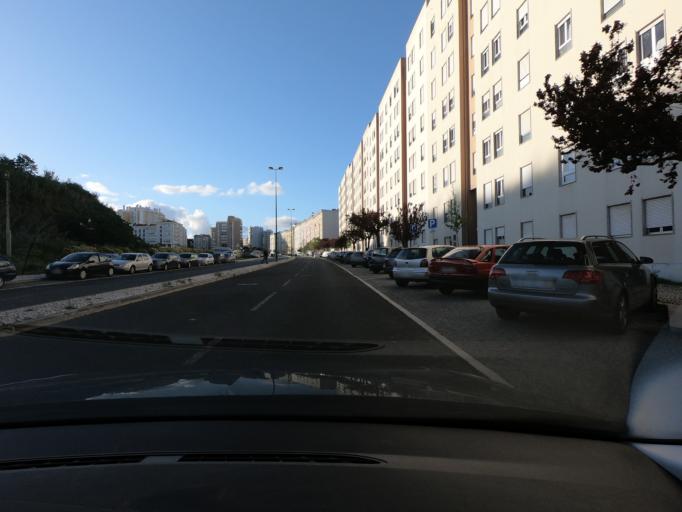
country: PT
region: Lisbon
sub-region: Lisbon
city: Lisbon
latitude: 38.7242
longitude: -9.1219
